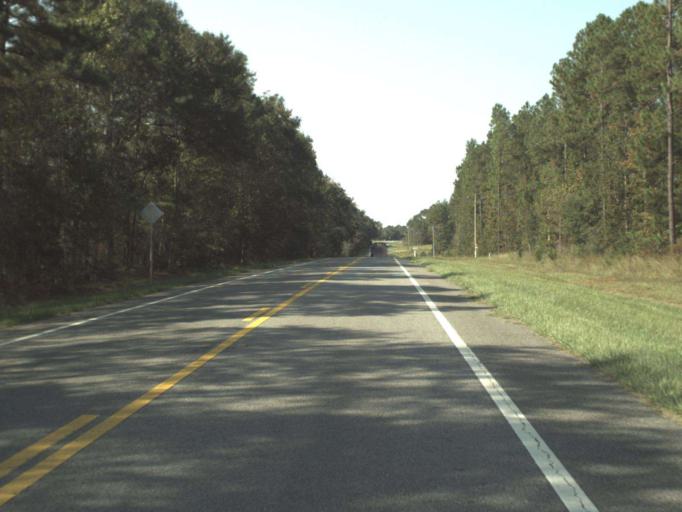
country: US
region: Alabama
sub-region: Geneva County
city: Geneva
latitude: 30.9555
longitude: -85.9090
